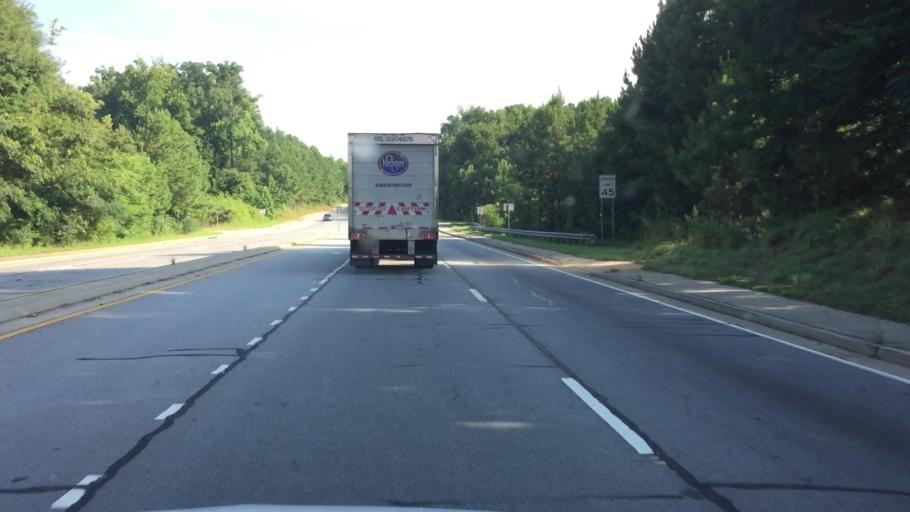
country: US
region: Georgia
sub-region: Rockdale County
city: Lakeview Estates
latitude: 33.7812
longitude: -84.0473
